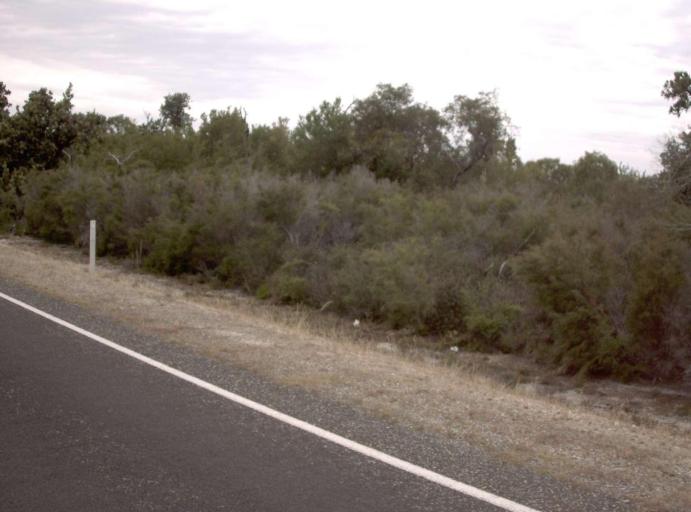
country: AU
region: Victoria
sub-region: Wellington
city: Sale
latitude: -38.1889
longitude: 147.3692
